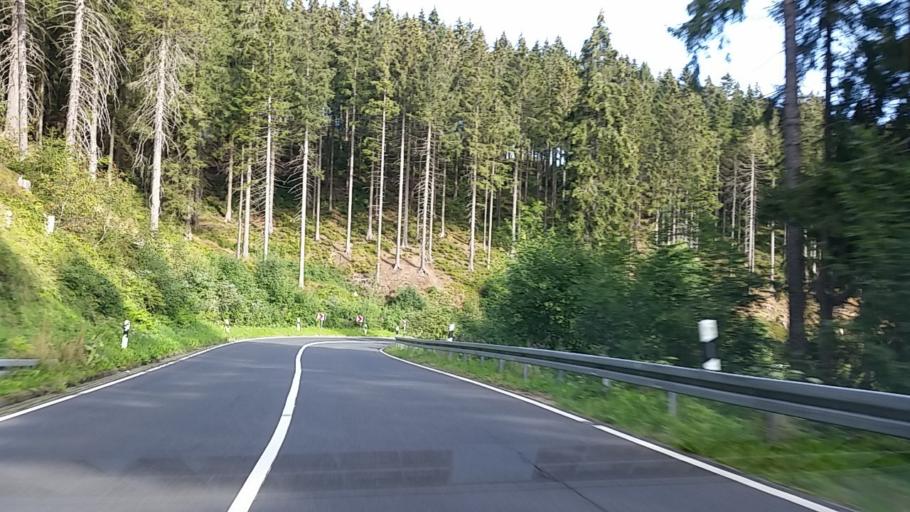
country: DE
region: Lower Saxony
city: Clausthal-Zellerfeld
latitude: 51.8571
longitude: 10.3646
